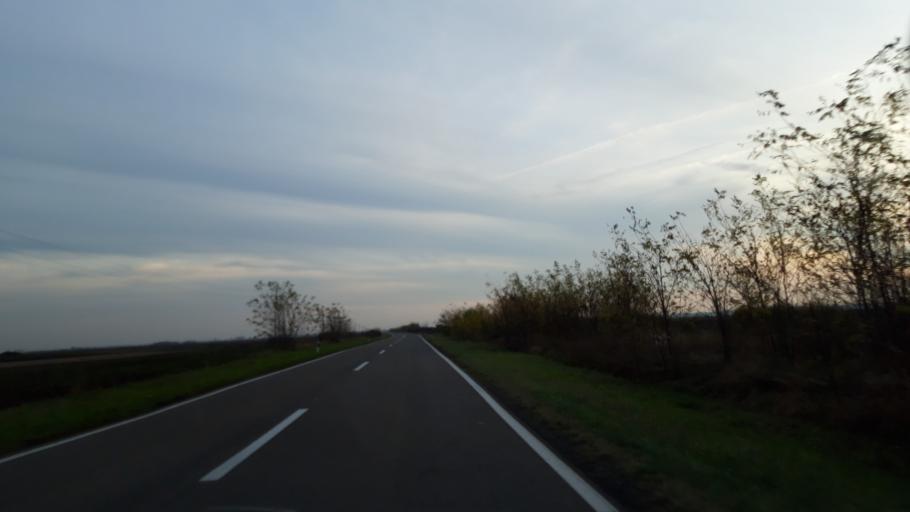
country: RS
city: Ostojicevo
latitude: 45.8640
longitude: 20.1647
